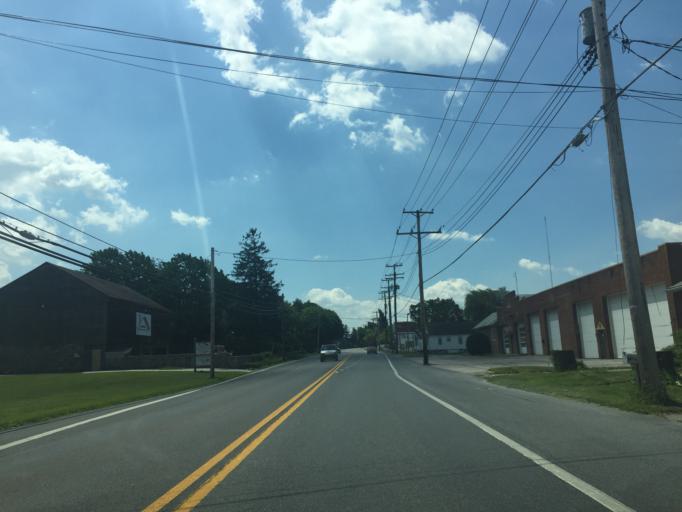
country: US
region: Maryland
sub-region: Carroll County
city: Hampstead
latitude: 39.6258
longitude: -76.8600
